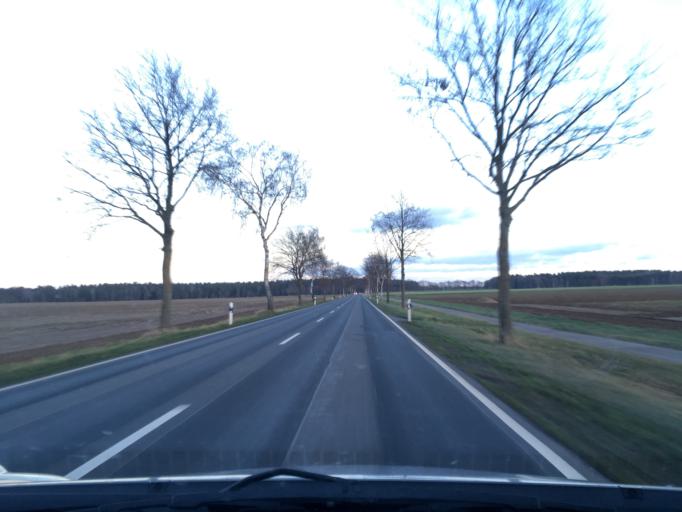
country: DE
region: Lower Saxony
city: Ratzlingen
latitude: 52.9798
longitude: 10.7048
